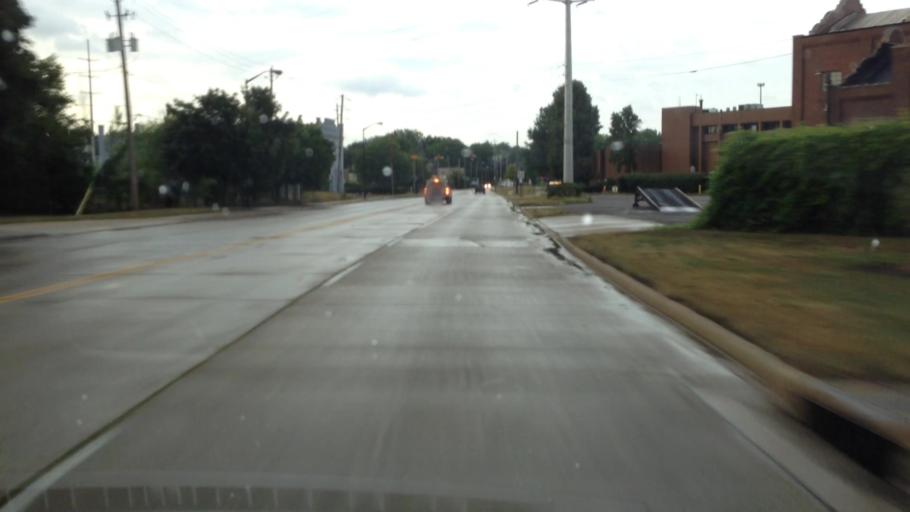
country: US
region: Ohio
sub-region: Summit County
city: Akron
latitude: 41.0491
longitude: -81.5425
